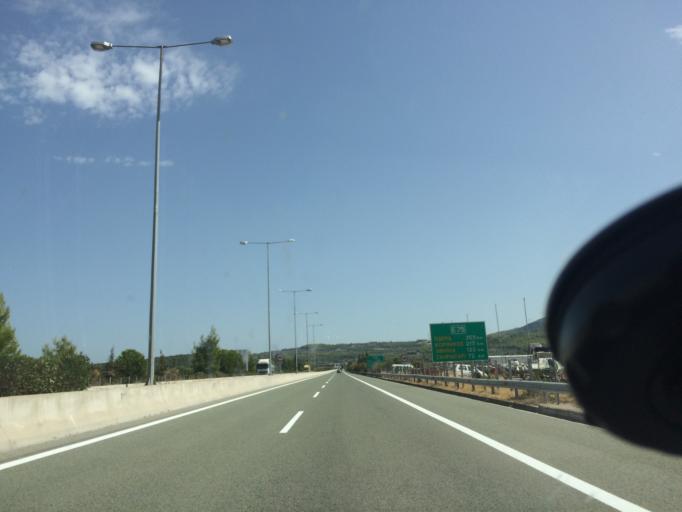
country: GR
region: Central Greece
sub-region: Nomos Fthiotidos
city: Martinon
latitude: 38.6206
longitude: 23.1312
